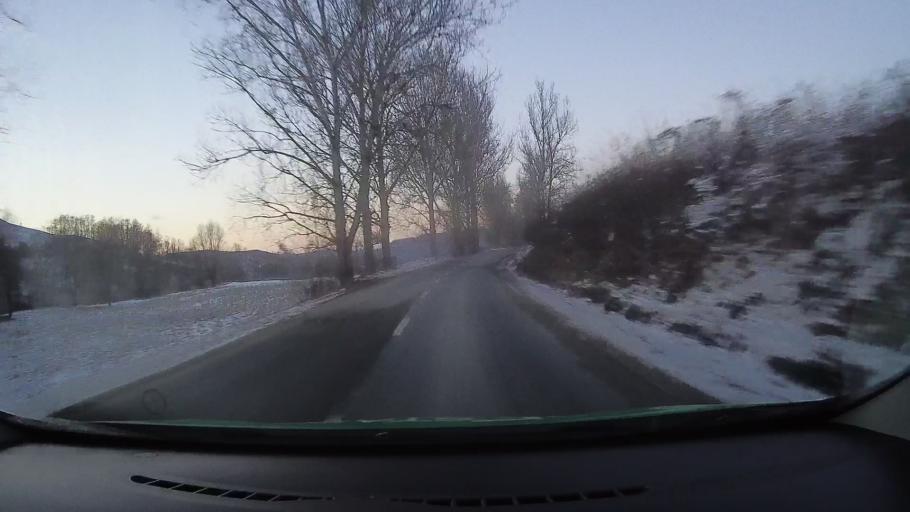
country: RO
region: Sibiu
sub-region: Comuna Alma
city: Alma
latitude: 46.1852
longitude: 24.4715
